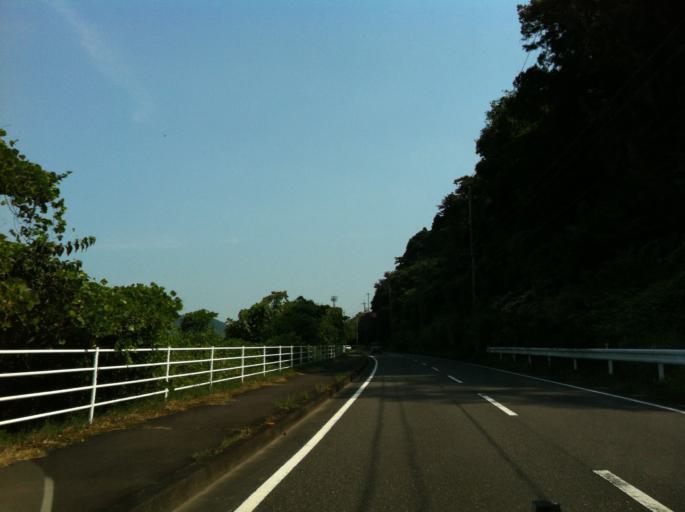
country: JP
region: Shizuoka
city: Shizuoka-shi
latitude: 35.0551
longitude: 138.3640
